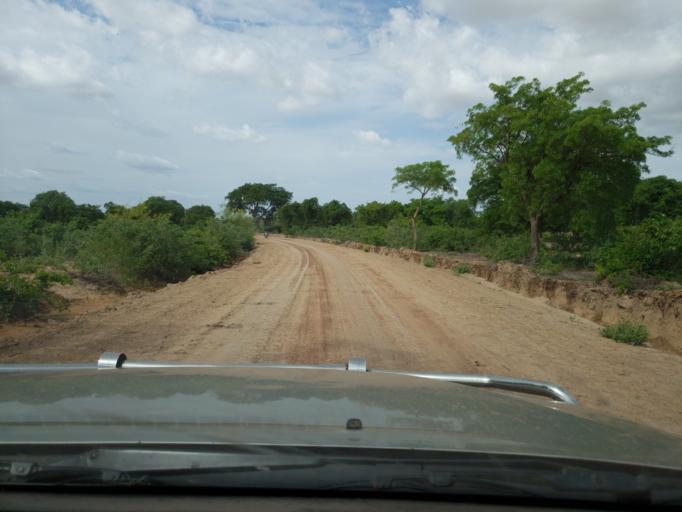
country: ML
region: Segou
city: Bla
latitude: 12.7126
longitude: -5.6866
